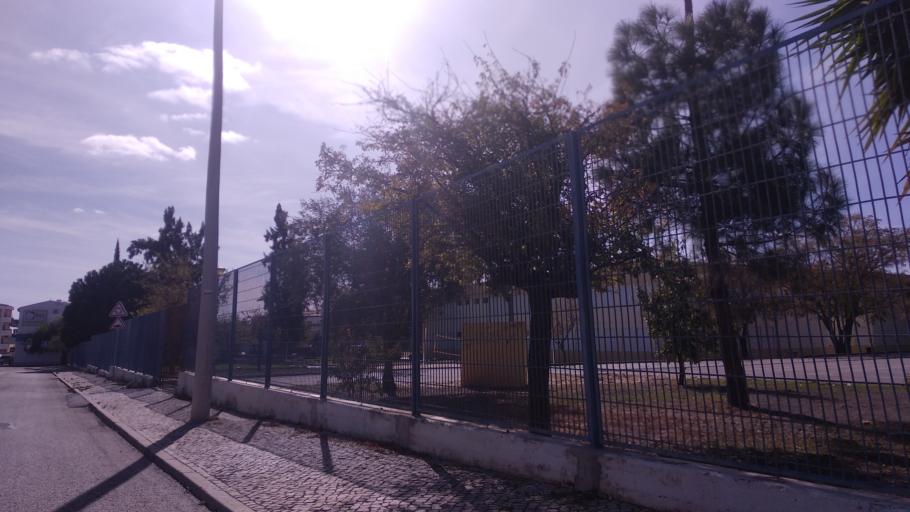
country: PT
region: Faro
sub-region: Sao Bras de Alportel
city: Sao Bras de Alportel
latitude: 37.1579
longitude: -7.8855
